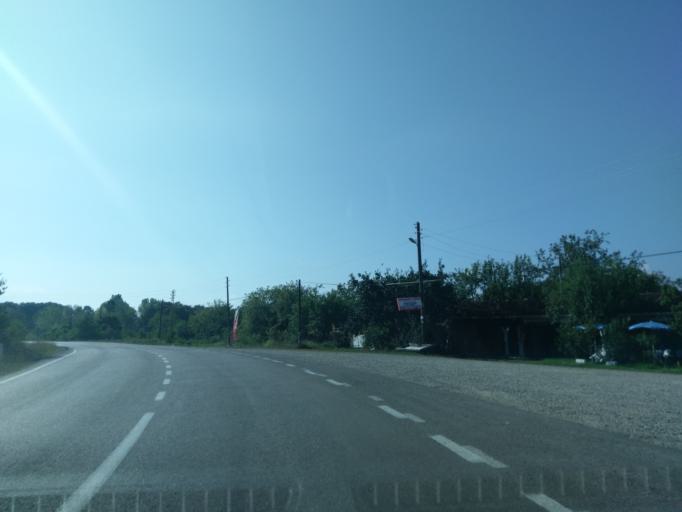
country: TR
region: Sinop
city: Yenikonak
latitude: 41.9465
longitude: 34.7565
